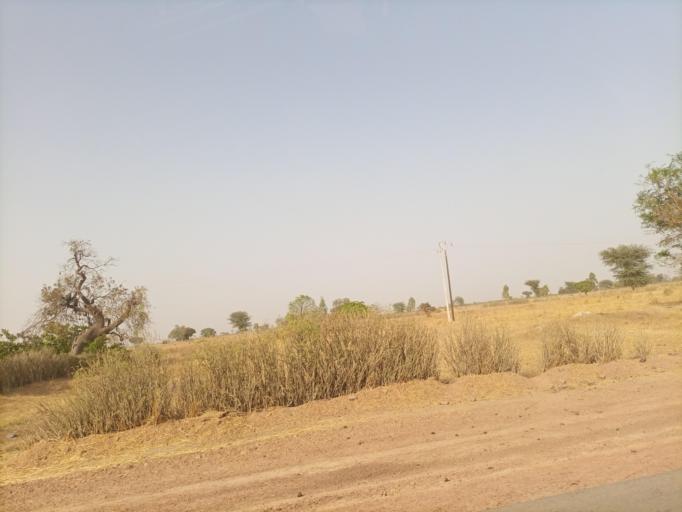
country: SN
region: Fatick
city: Passi
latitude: 14.0298
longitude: -16.3089
